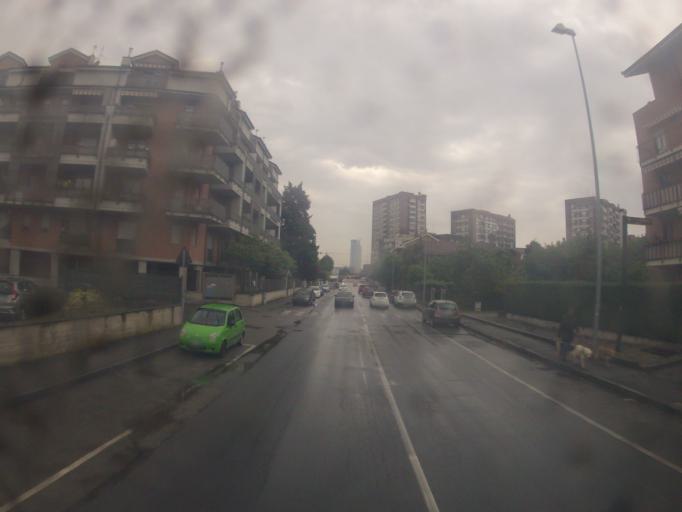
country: IT
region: Piedmont
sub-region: Provincia di Torino
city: Moncalieri
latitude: 45.0053
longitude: 7.6697
